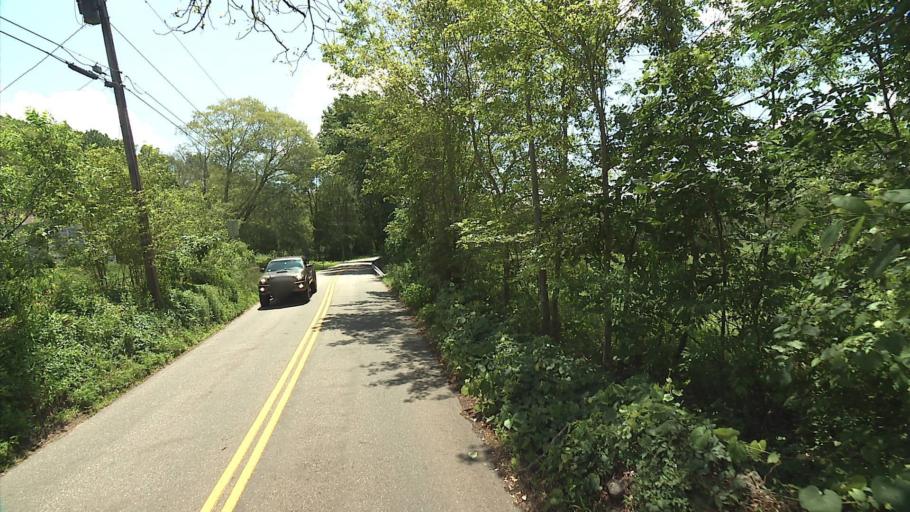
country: US
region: Connecticut
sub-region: New London County
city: Jewett City
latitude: 41.5989
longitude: -71.9043
